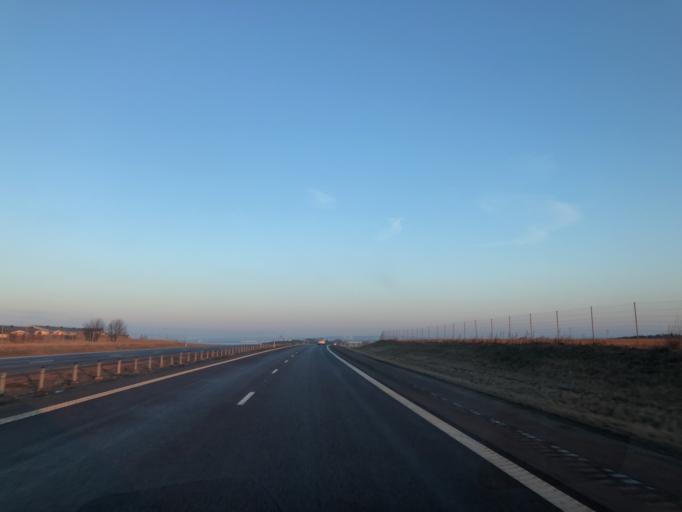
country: SE
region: Halland
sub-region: Halmstads Kommun
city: Paarp
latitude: 56.6031
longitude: 12.9247
